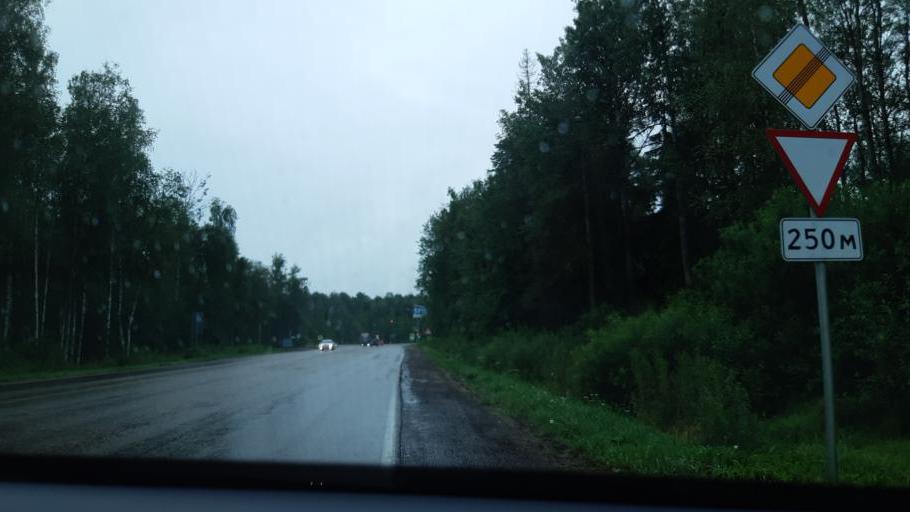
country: RU
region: Smolensk
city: Gagarin
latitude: 55.5019
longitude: 35.0363
